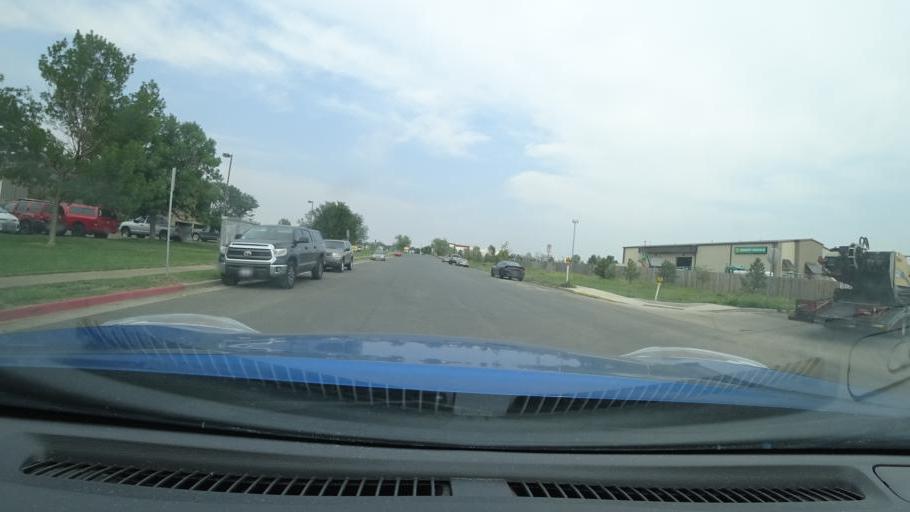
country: US
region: Colorado
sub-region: Adams County
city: Aurora
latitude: 39.7492
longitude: -104.7771
